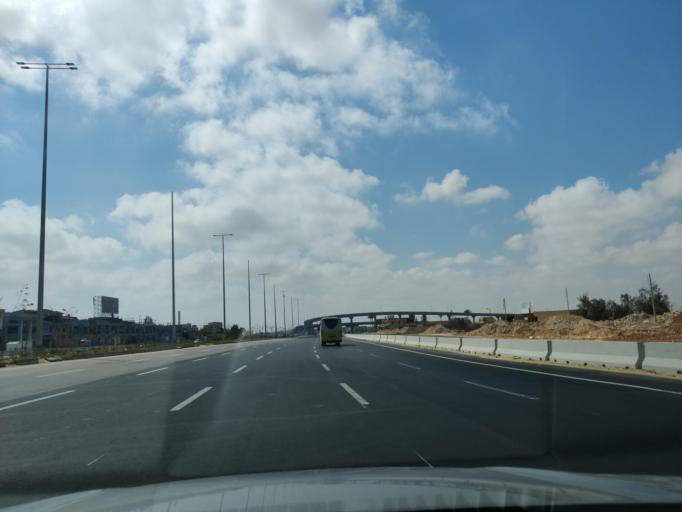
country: EG
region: Muhafazat Matruh
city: Al `Alamayn
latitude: 30.9558
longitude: 28.7666
